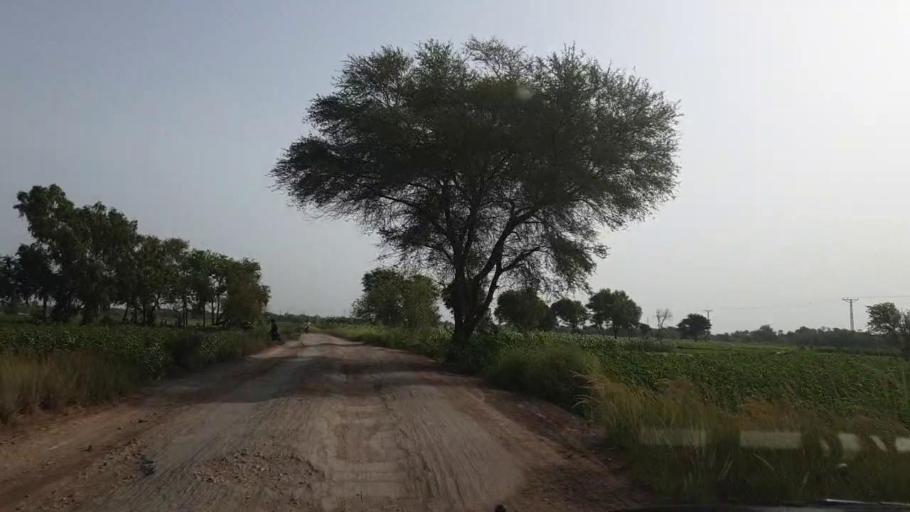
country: PK
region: Sindh
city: Nawabshah
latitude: 26.2223
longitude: 68.4051
